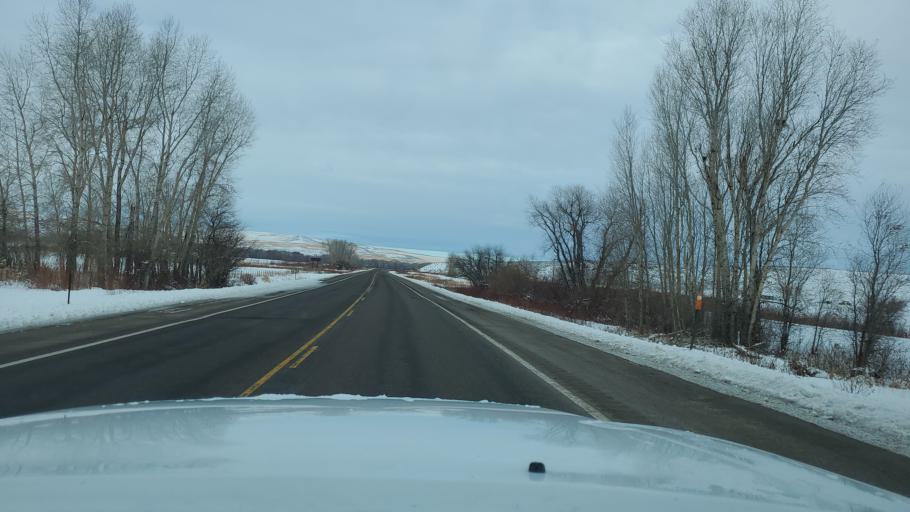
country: US
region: Colorado
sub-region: Routt County
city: Hayden
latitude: 40.4933
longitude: -107.3509
